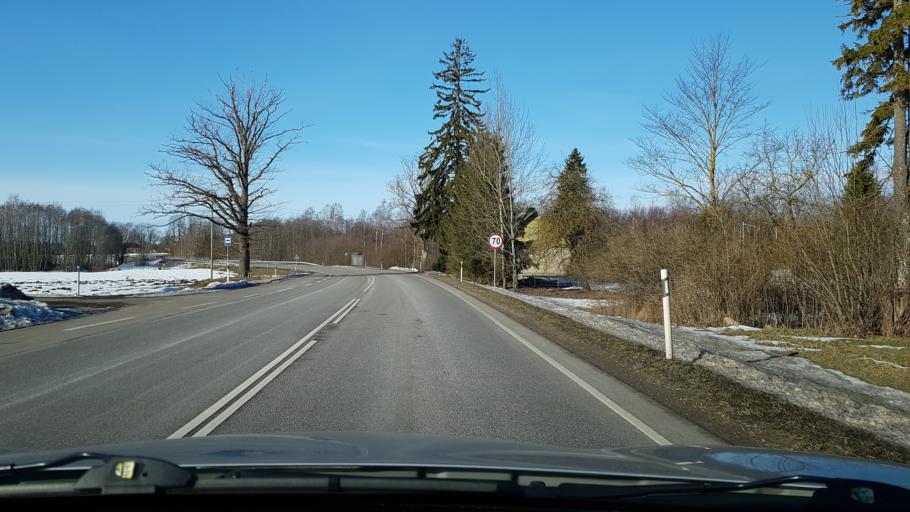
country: EE
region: Viljandimaa
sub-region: Vohma linn
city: Vohma
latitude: 58.6367
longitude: 25.6928
